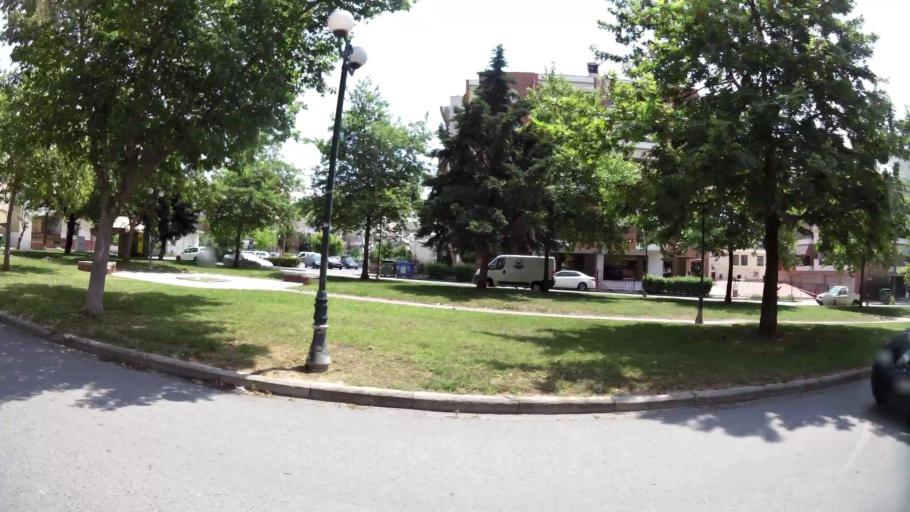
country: GR
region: Central Macedonia
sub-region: Nomos Thessalonikis
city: Evosmos
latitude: 40.6681
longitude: 22.9043
